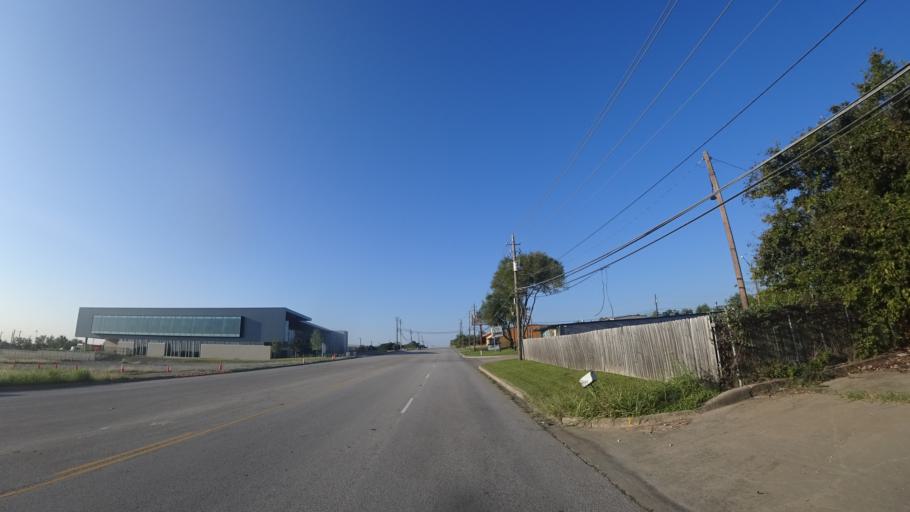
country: US
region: Texas
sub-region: Travis County
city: Austin
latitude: 30.3225
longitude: -97.6590
